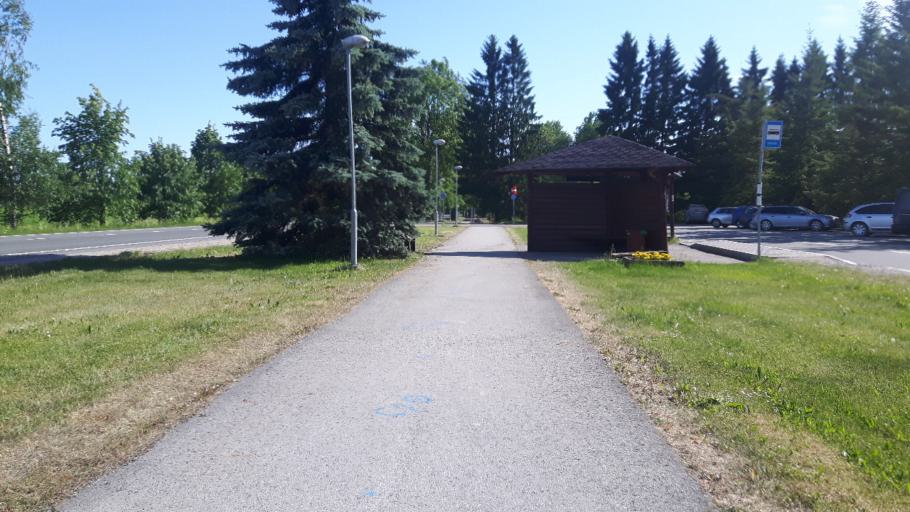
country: EE
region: Raplamaa
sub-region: Kehtna vald
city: Kehtna
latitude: 58.9284
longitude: 24.8771
